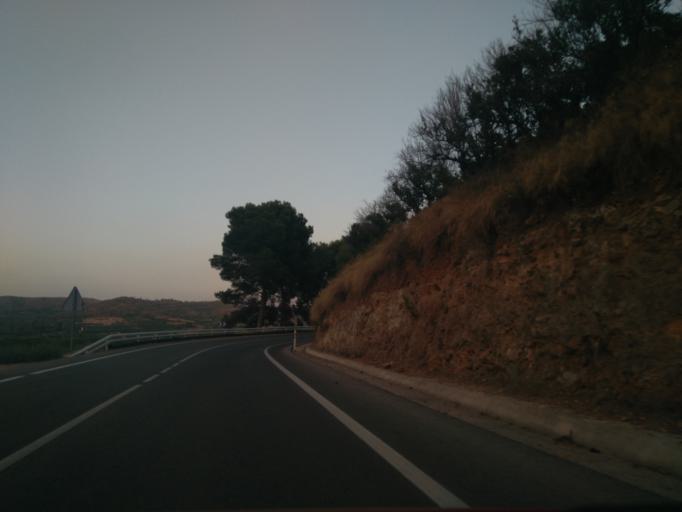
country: ES
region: Valencia
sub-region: Provincia de Valencia
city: Sumacarcer
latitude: 39.0869
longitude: -0.6252
